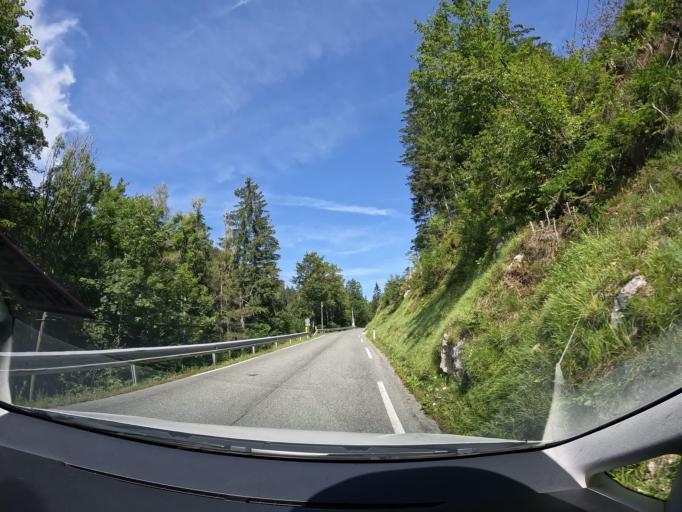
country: AT
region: Carinthia
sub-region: Politischer Bezirk Villach Land
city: Sankt Jakob
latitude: 46.5589
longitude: 14.0774
